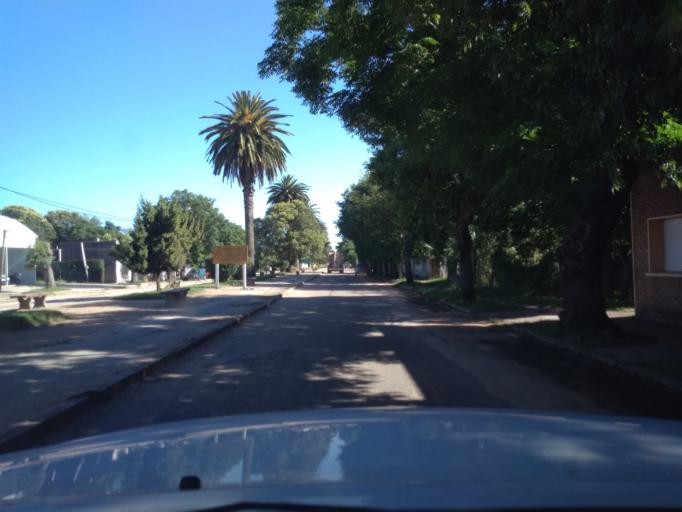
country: UY
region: Canelones
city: San Ramon
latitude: -34.2987
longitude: -55.9577
